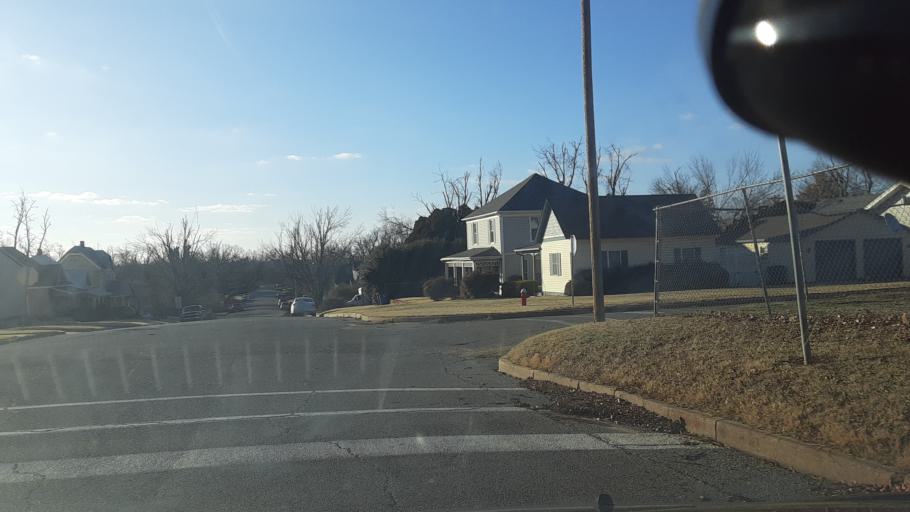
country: US
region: Oklahoma
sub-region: Logan County
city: Guthrie
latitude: 35.8823
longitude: -97.4200
